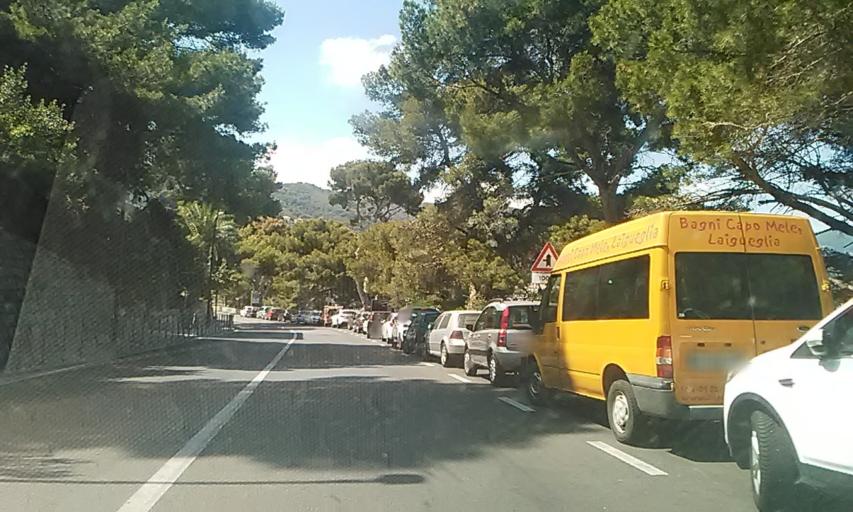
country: IT
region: Liguria
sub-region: Provincia di Savona
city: Laigueglia
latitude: 43.9681
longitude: 8.1637
